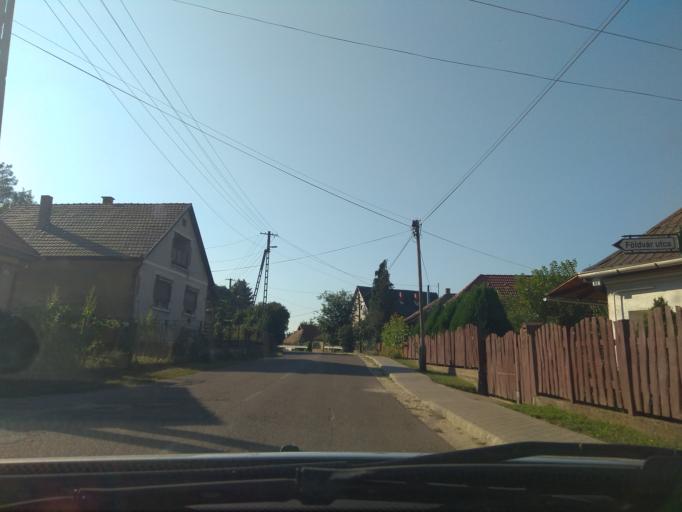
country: HU
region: Borsod-Abauj-Zemplen
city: Harsany
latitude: 47.9874
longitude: 20.7782
